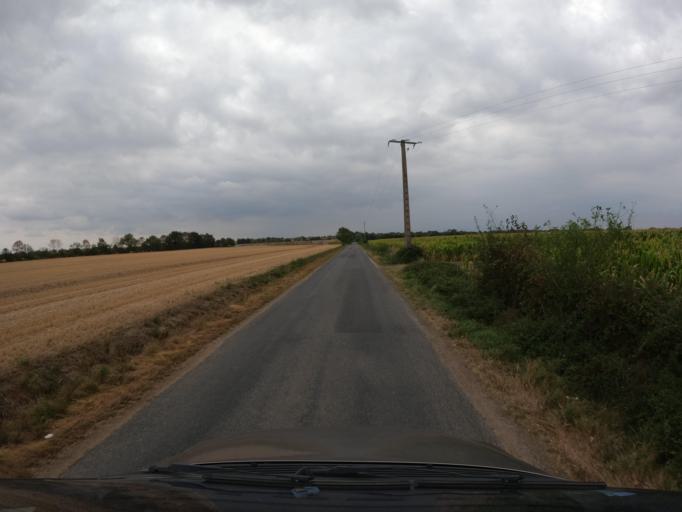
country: FR
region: Pays de la Loire
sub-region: Departement de la Vendee
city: La Bruffiere
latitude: 46.9898
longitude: -1.1593
